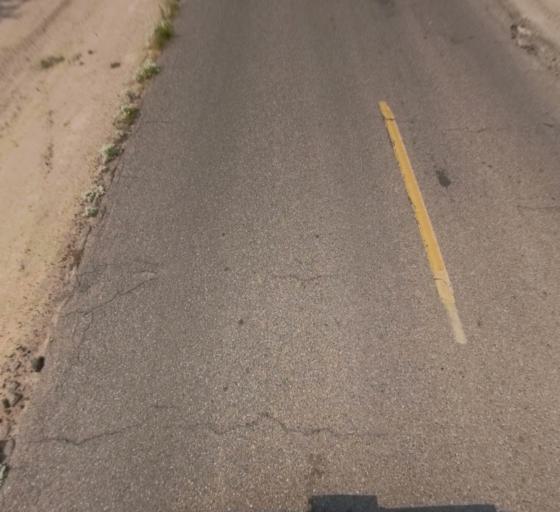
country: US
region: California
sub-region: Madera County
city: Madera Acres
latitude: 37.0574
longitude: -120.1107
